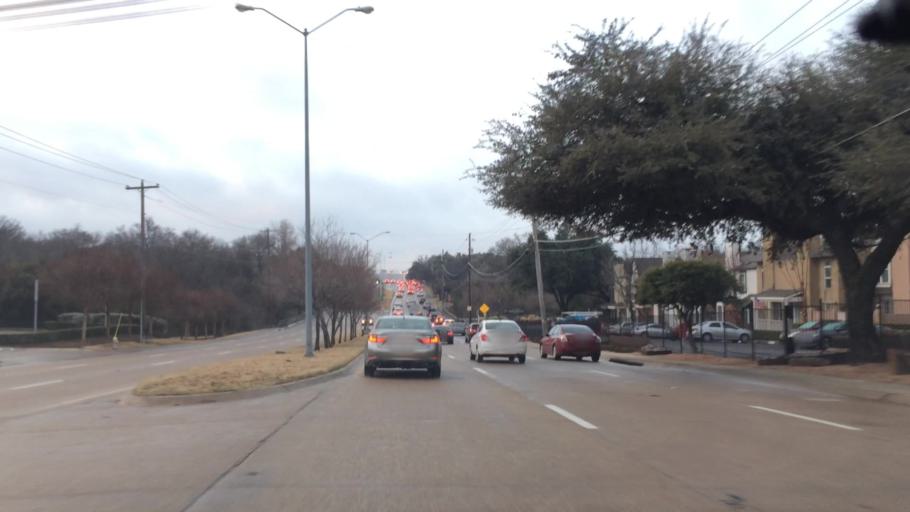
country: US
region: Texas
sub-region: Dallas County
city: Addison
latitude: 32.9661
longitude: -96.8045
